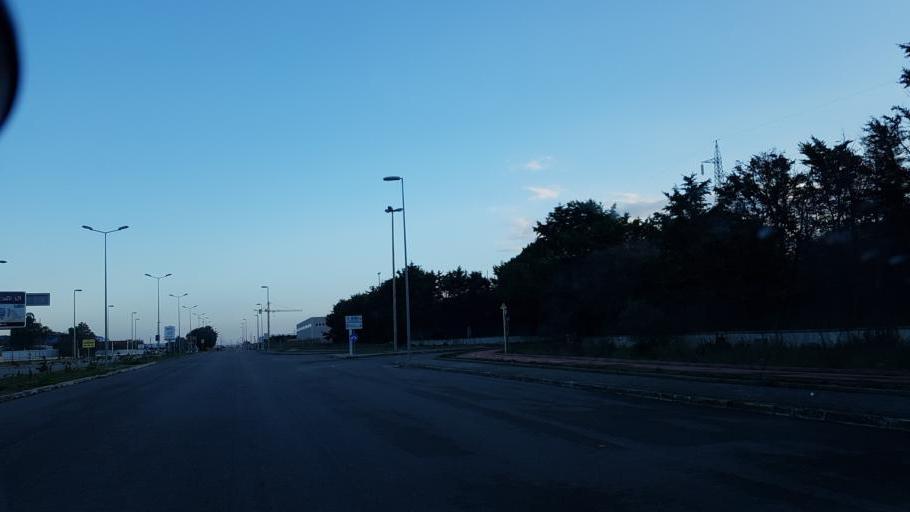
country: IT
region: Apulia
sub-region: Provincia di Lecce
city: Surbo
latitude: 40.3796
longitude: 18.1260
